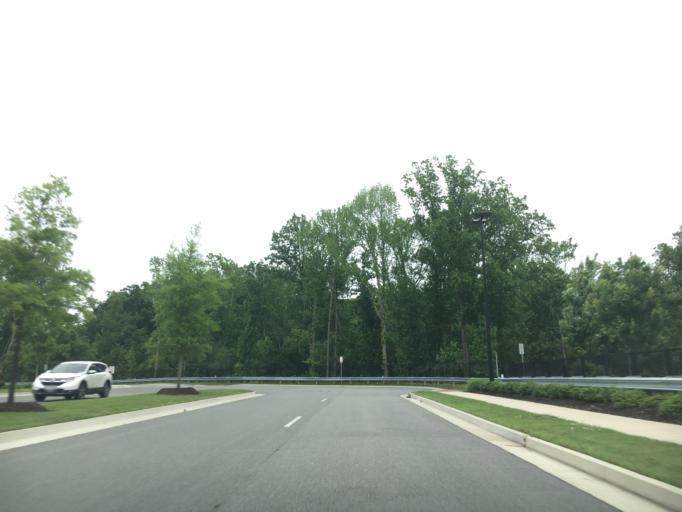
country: US
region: Virginia
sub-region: Henrico County
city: Short Pump
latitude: 37.6619
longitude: -77.6363
